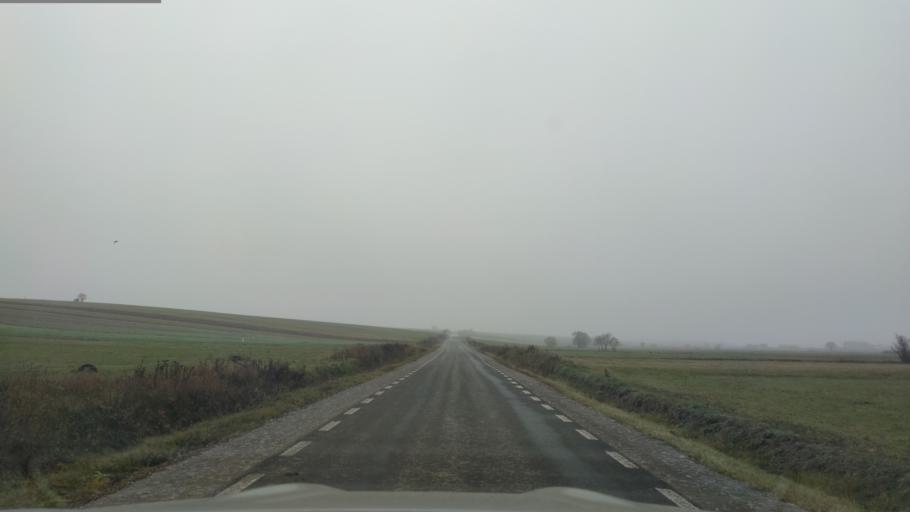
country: RO
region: Harghita
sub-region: Comuna Remetea
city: Remetea
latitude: 46.8054
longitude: 25.4303
